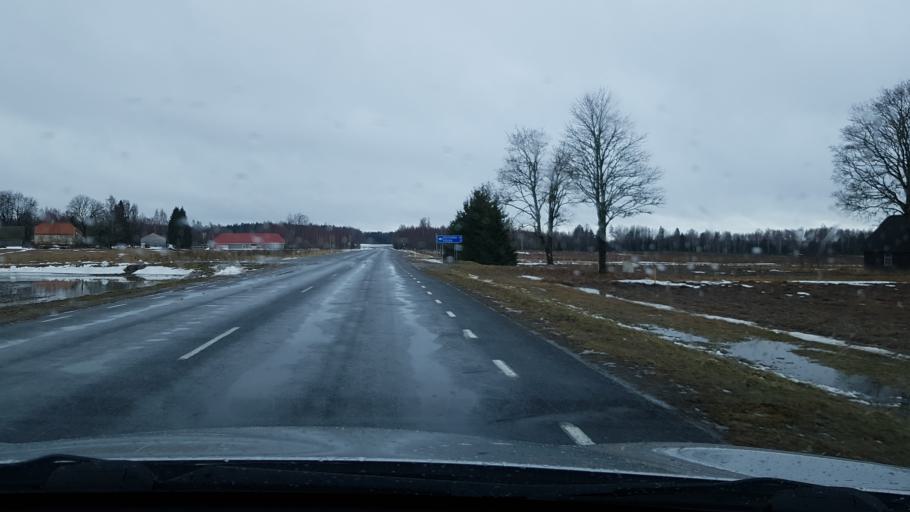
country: LV
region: Apes Novads
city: Ape
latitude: 57.6826
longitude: 26.7251
